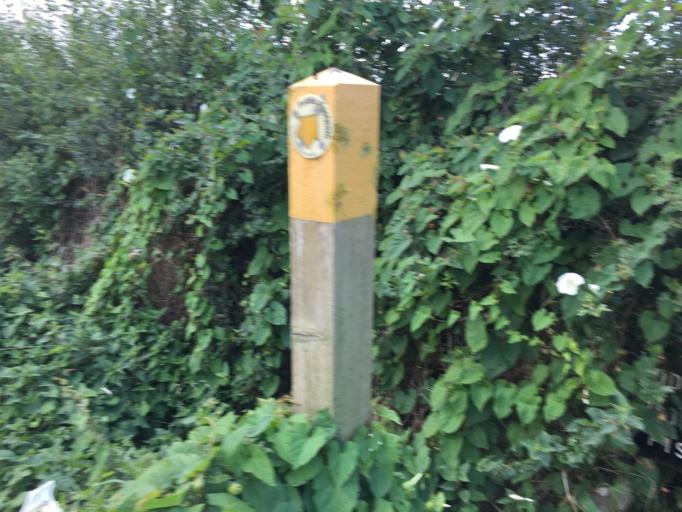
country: GB
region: England
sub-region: Warwickshire
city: Long Itchington
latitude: 52.3196
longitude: -1.4059
